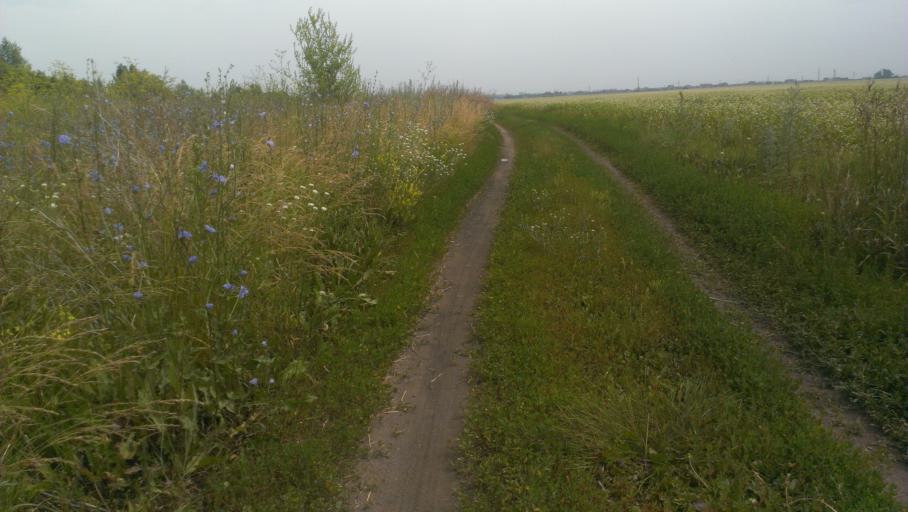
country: RU
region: Altai Krai
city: Gon'ba
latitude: 53.3797
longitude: 83.6333
